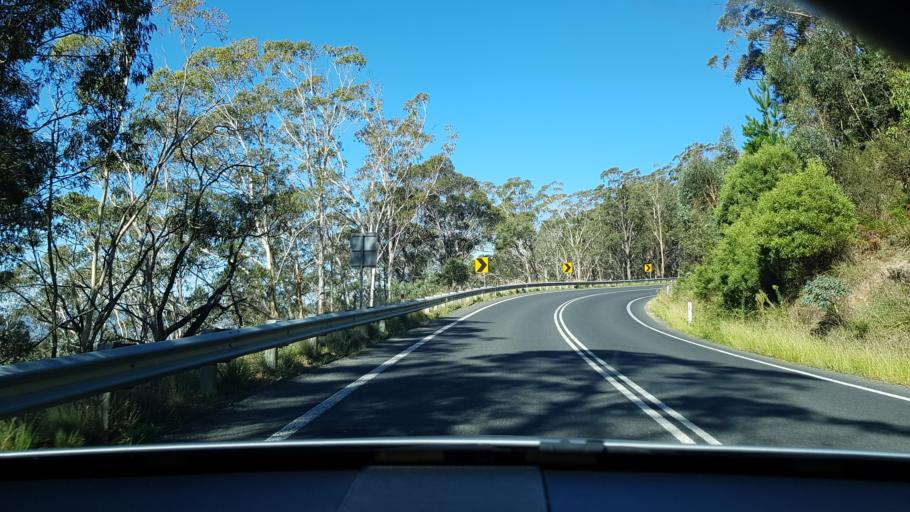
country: AU
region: New South Wales
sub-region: Lithgow
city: Bowenfels
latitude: -33.6689
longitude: 150.0502
